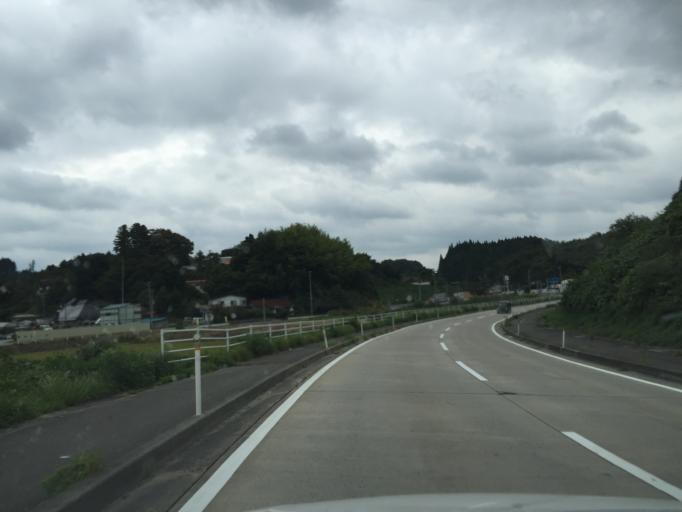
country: JP
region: Fukushima
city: Miharu
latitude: 37.4468
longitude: 140.5177
